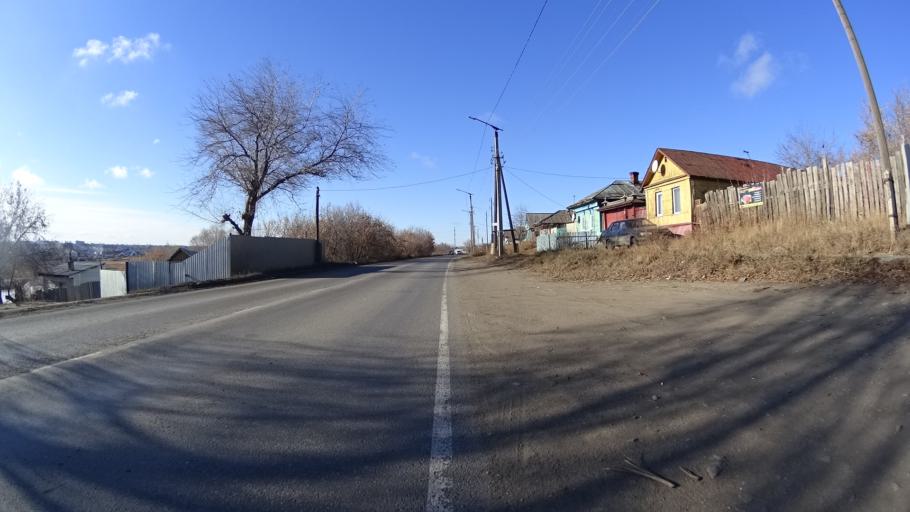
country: RU
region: Chelyabinsk
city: Troitsk
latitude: 54.0967
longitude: 61.5544
